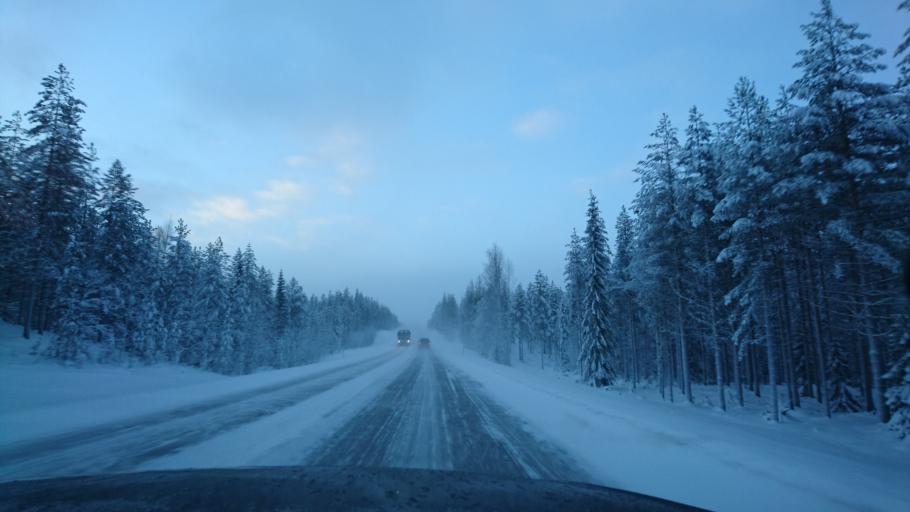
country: FI
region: Northern Ostrobothnia
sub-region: Koillismaa
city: Taivalkoski
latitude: 65.4822
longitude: 27.8037
